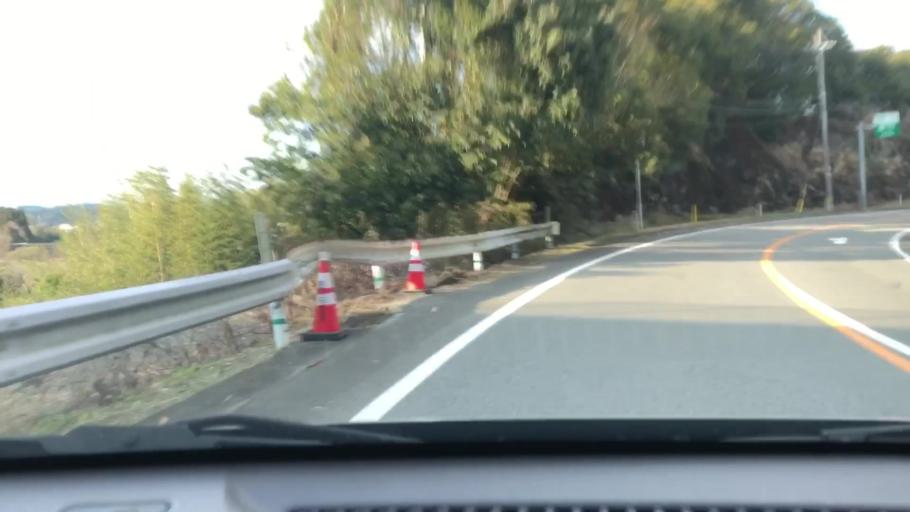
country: JP
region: Miyazaki
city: Miyazaki-shi
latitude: 31.8201
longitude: 131.2962
